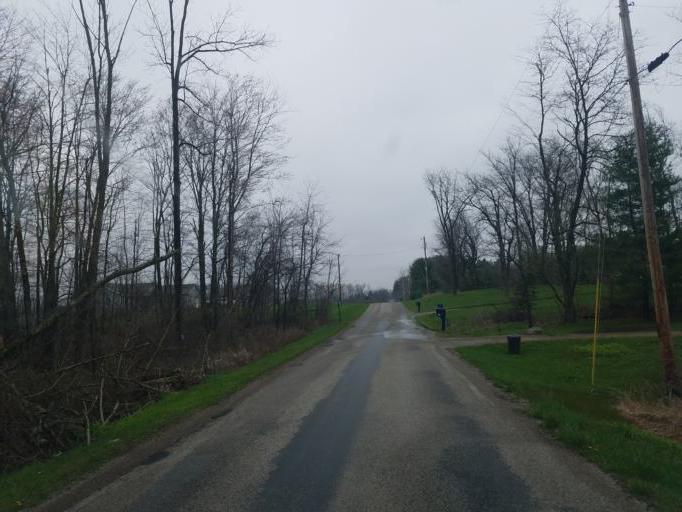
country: US
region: Ohio
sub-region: Morrow County
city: Mount Gilead
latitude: 40.6131
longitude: -82.8042
